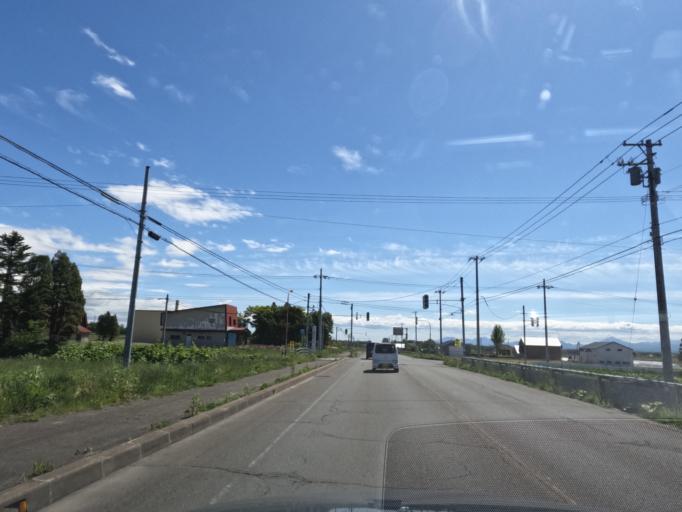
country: JP
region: Hokkaido
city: Kitahiroshima
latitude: 43.0312
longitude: 141.7147
